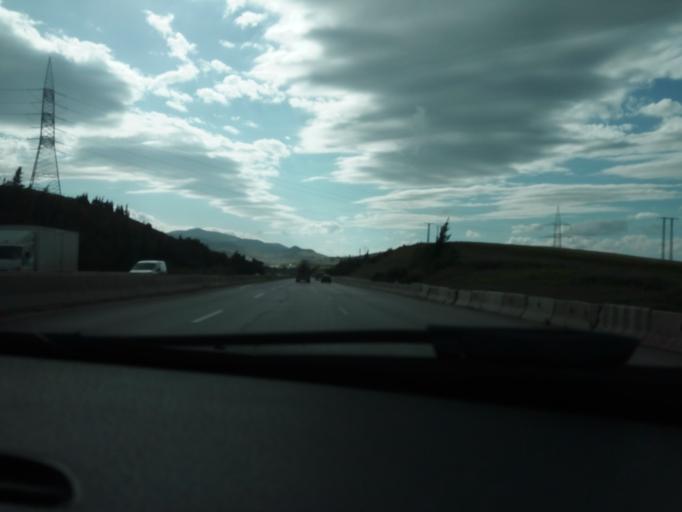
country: DZ
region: Tipaza
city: El Affroun
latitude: 36.4466
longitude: 2.6064
